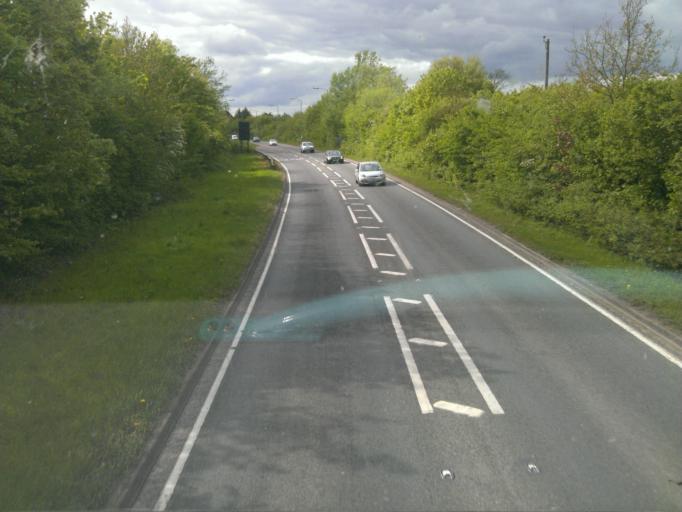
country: GB
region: England
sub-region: Essex
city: Coggeshall
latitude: 51.8789
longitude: 0.6968
